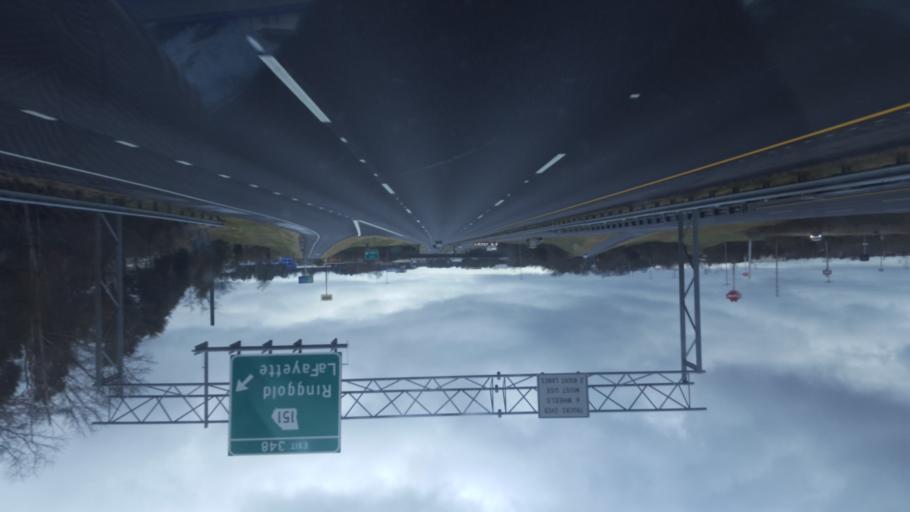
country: US
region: Georgia
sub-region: Catoosa County
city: Ringgold
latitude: 34.9095
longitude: -85.1225
